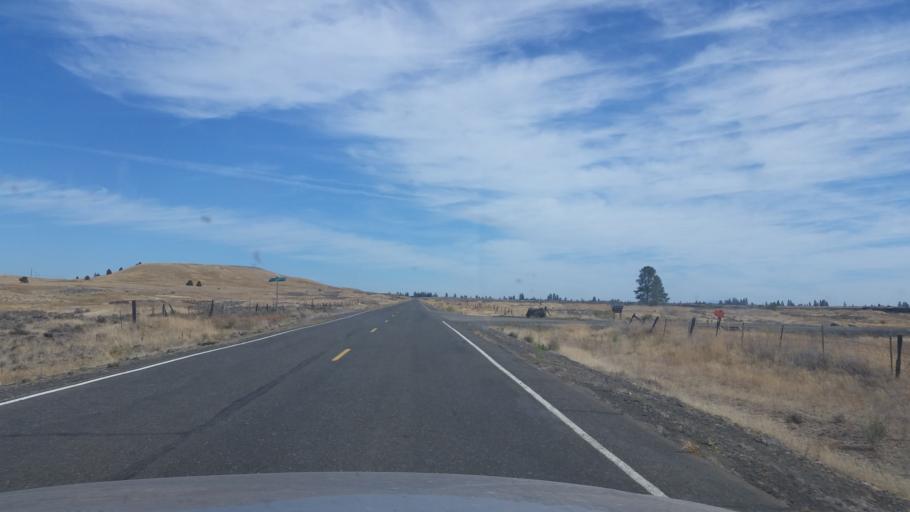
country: US
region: Washington
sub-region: Spokane County
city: Medical Lake
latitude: 47.3470
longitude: -117.8638
